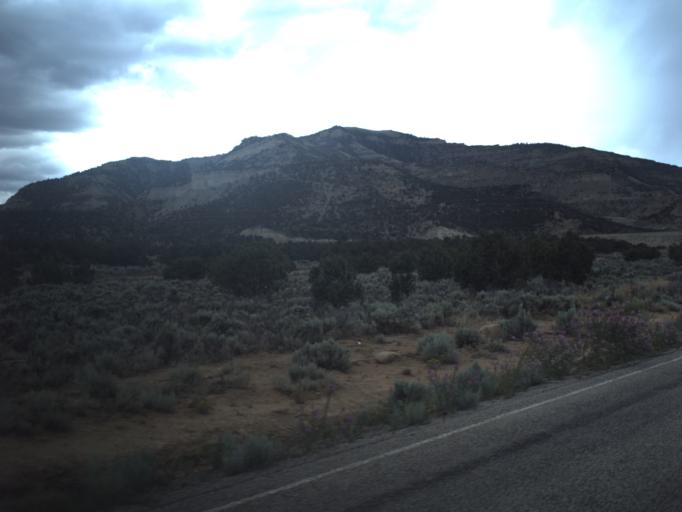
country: US
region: Utah
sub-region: Emery County
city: Huntington
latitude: 39.4842
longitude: -110.9896
